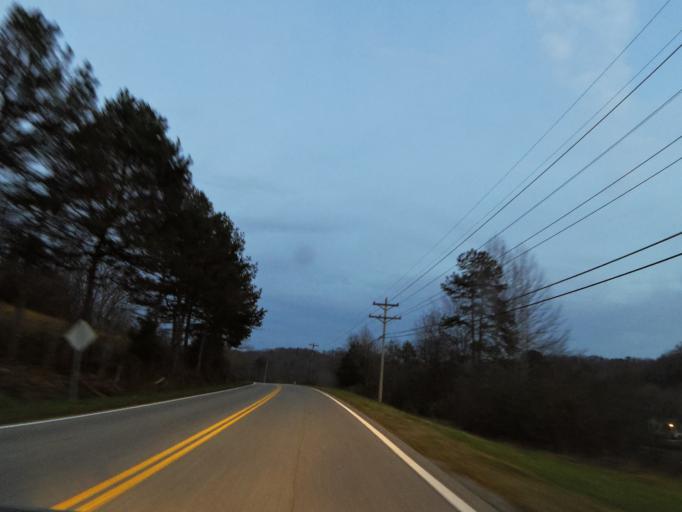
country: US
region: Tennessee
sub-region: Morgan County
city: Coalfield
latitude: 35.9788
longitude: -84.4421
